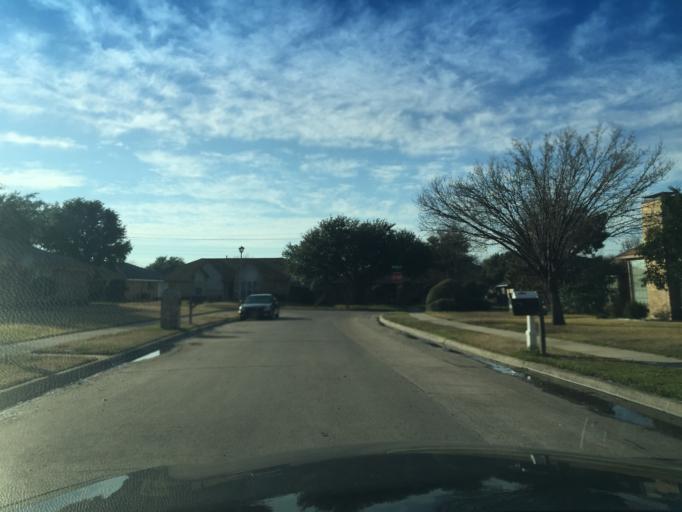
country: US
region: Texas
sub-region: Dallas County
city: Carrollton
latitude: 32.9882
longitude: -96.8740
